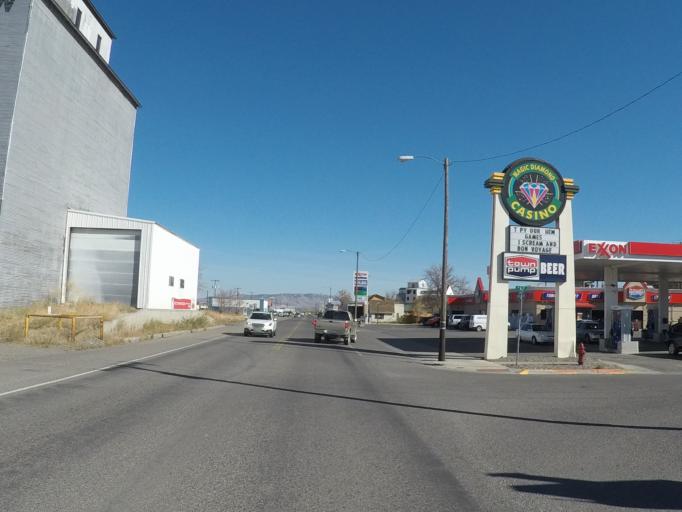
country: US
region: Montana
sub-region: Park County
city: Livingston
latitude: 45.6661
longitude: -110.5543
